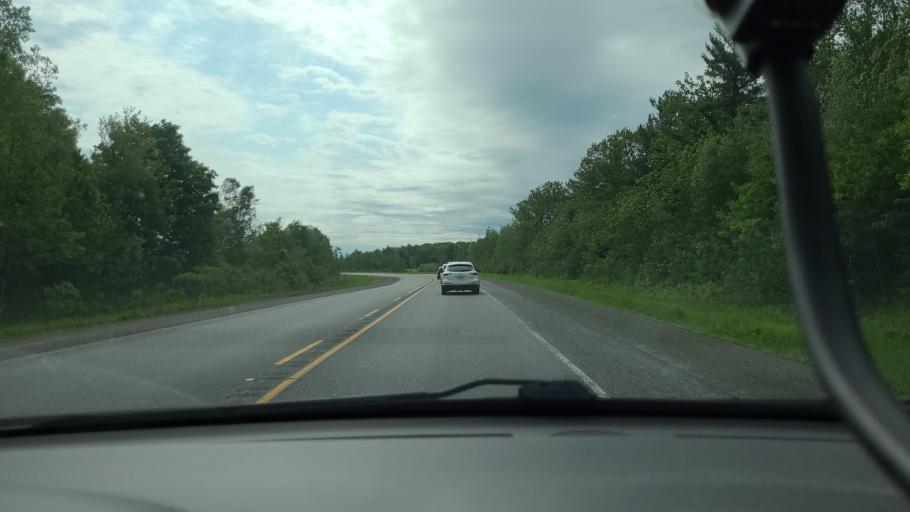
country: CA
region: Quebec
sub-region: Lanaudiere
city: Crabtree
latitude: 45.9618
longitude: -73.5123
